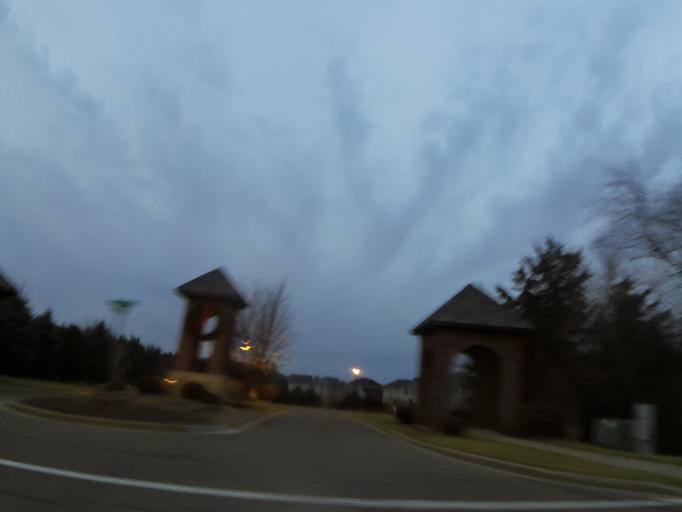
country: US
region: Wisconsin
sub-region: Saint Croix County
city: Hudson
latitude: 44.9490
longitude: -92.7062
